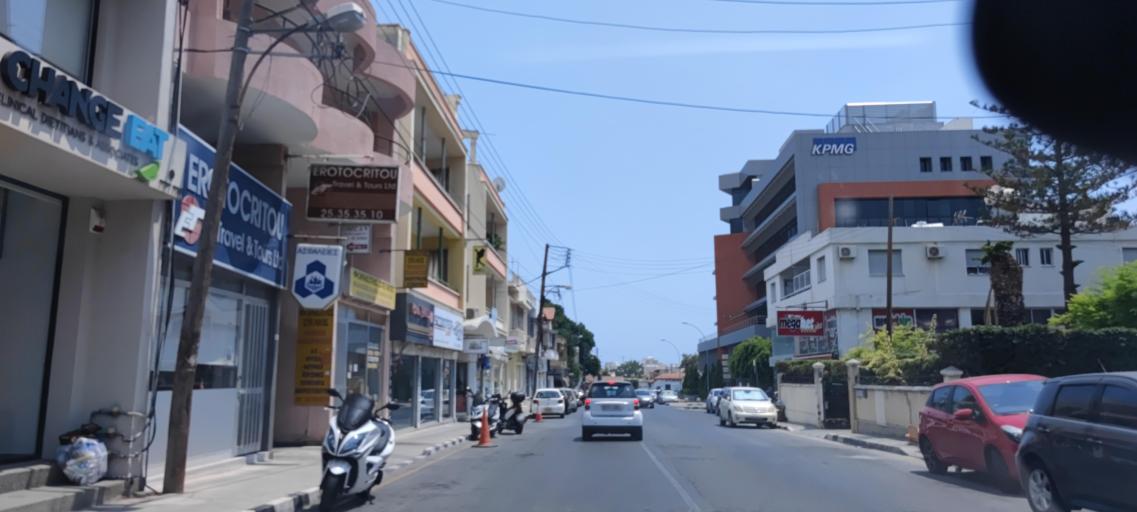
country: CY
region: Limassol
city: Limassol
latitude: 34.6802
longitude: 33.0402
